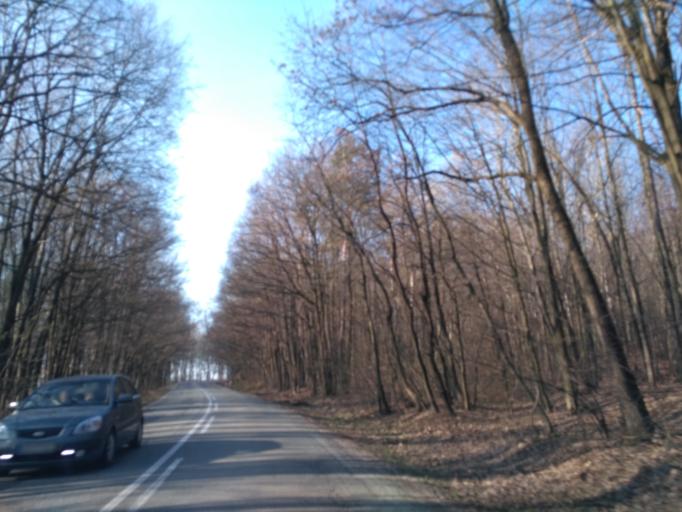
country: SK
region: Kosicky
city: Kosice
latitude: 48.6763
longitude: 21.1589
